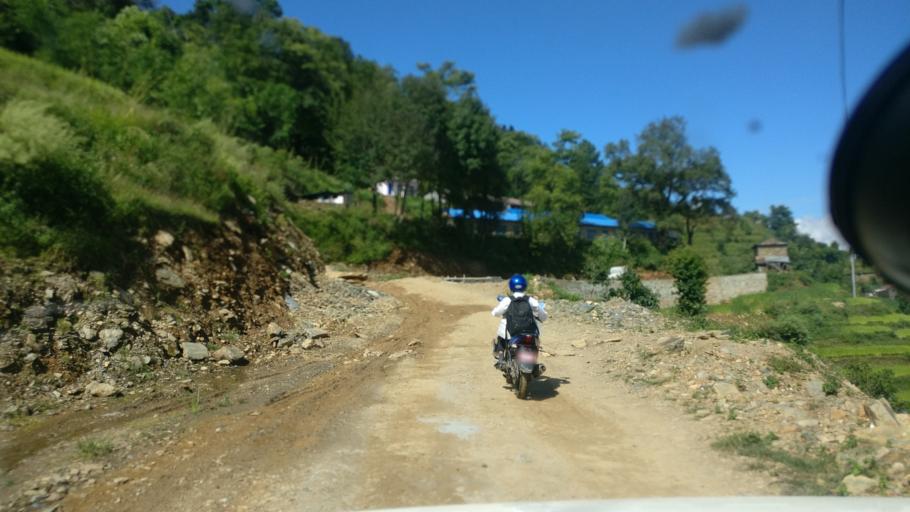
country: NP
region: Western Region
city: Baglung
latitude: 28.1253
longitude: 83.6682
